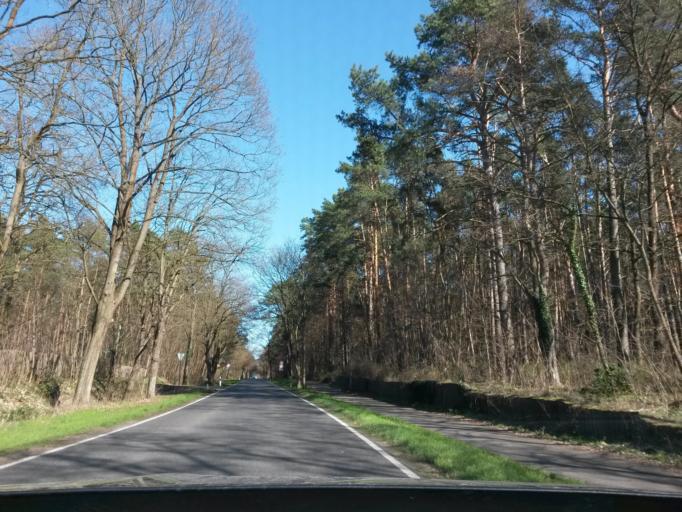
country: DE
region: Brandenburg
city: Rehfelde
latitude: 52.4533
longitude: 13.8826
